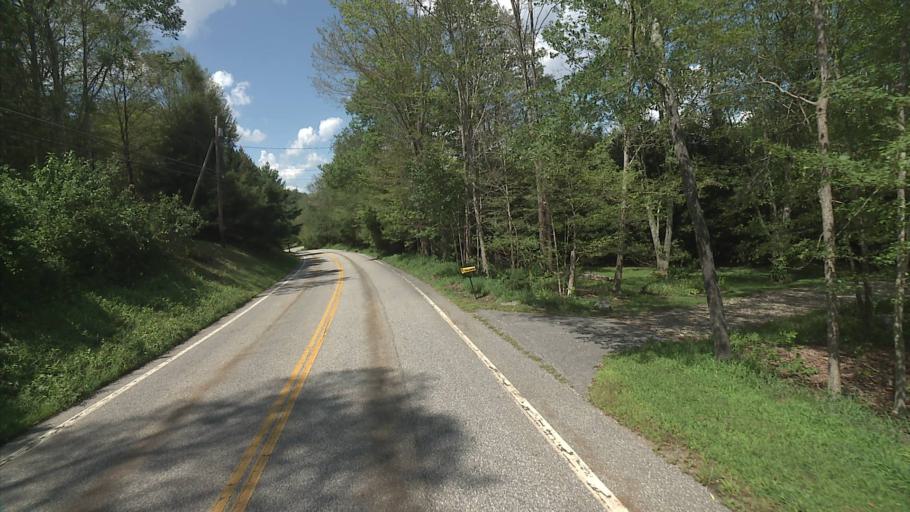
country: US
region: Connecticut
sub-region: Tolland County
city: Storrs
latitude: 41.8167
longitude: -72.1703
